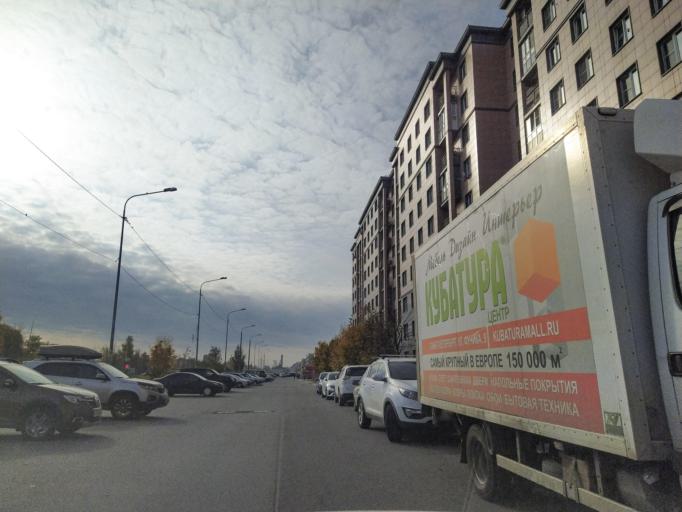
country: RU
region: St.-Petersburg
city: Tyarlevo
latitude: 59.7373
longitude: 30.4743
